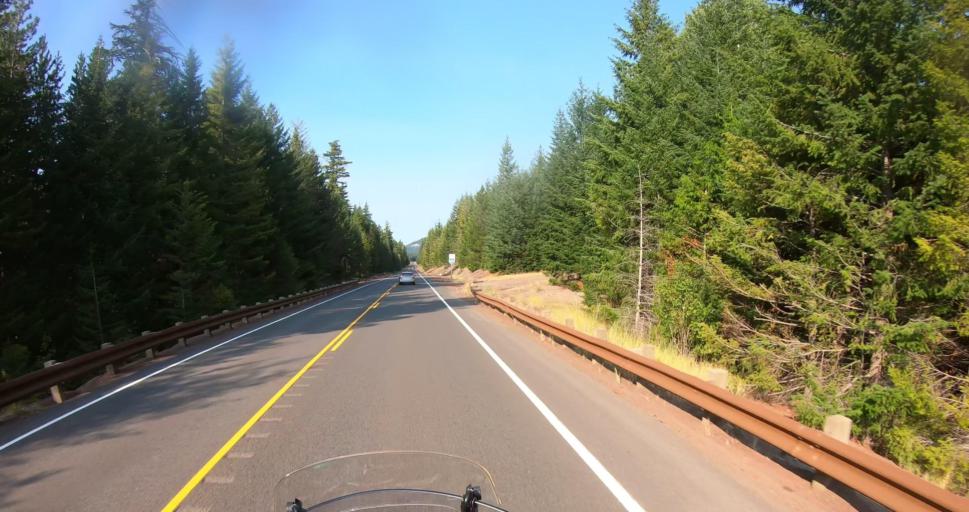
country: US
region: Oregon
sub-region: Hood River County
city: Odell
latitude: 45.3504
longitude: -121.5681
